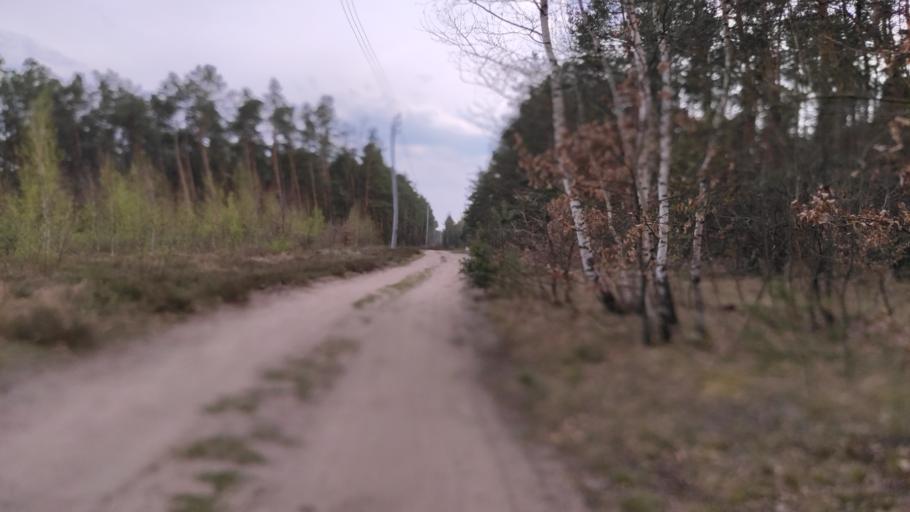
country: PL
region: Masovian Voivodeship
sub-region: Powiat grojecki
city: Warka
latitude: 51.7665
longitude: 21.1967
